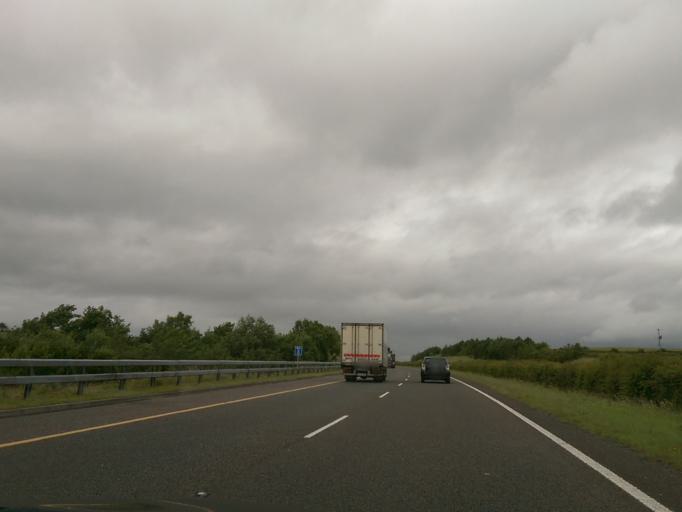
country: IE
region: Munster
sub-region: An Clar
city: Newmarket on Fergus
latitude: 52.7725
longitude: -8.9177
